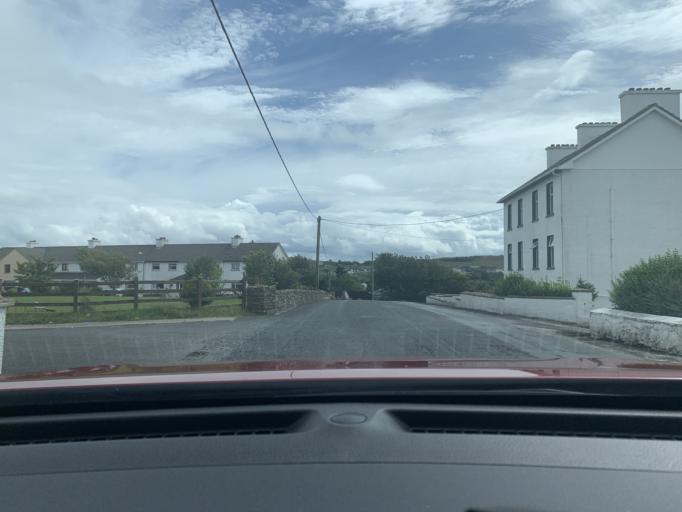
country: IE
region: Ulster
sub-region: County Donegal
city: Dungloe
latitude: 54.9530
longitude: -8.3633
